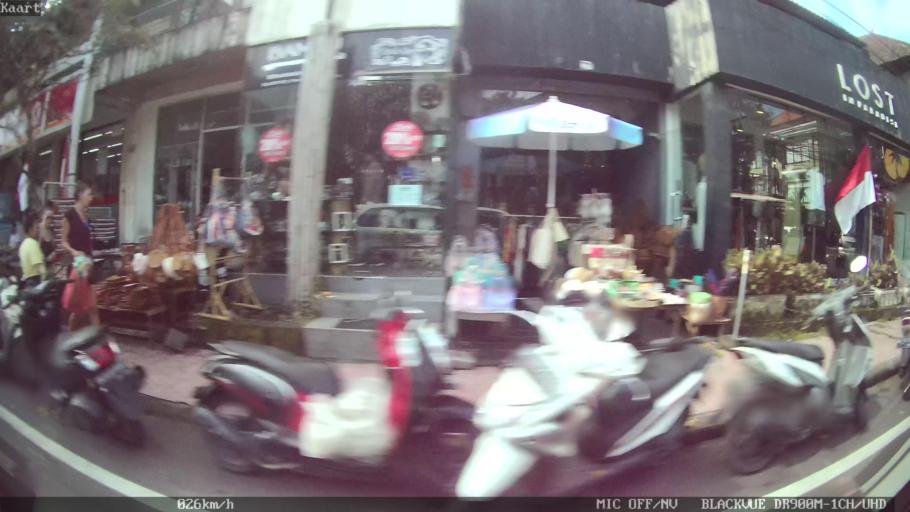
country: ID
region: Bali
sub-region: Kabupaten Gianyar
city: Ubud
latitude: -8.5076
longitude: 115.2656
